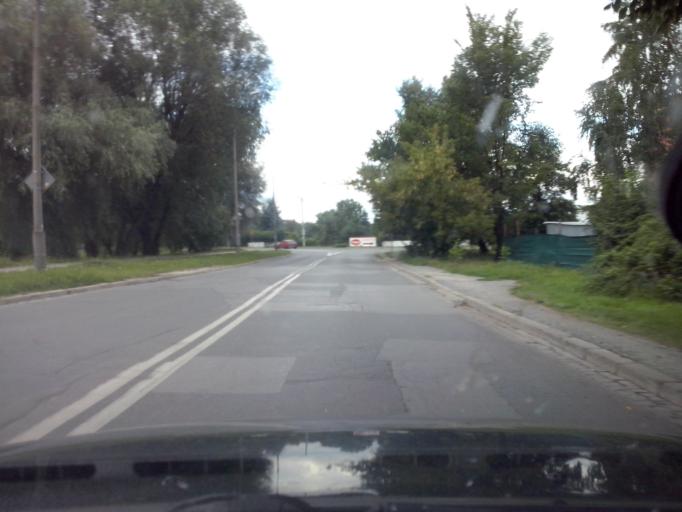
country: PL
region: Lesser Poland Voivodeship
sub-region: Krakow
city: Krakow
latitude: 50.0411
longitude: 19.9917
